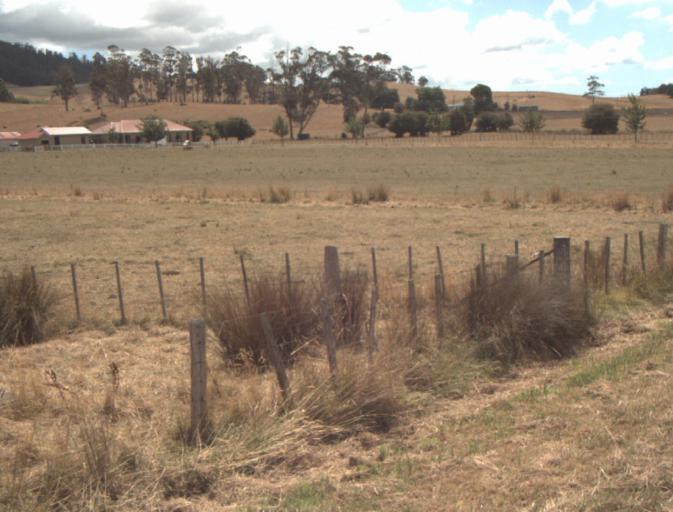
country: AU
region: Tasmania
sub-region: Launceston
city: Mayfield
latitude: -41.2337
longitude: 147.1254
